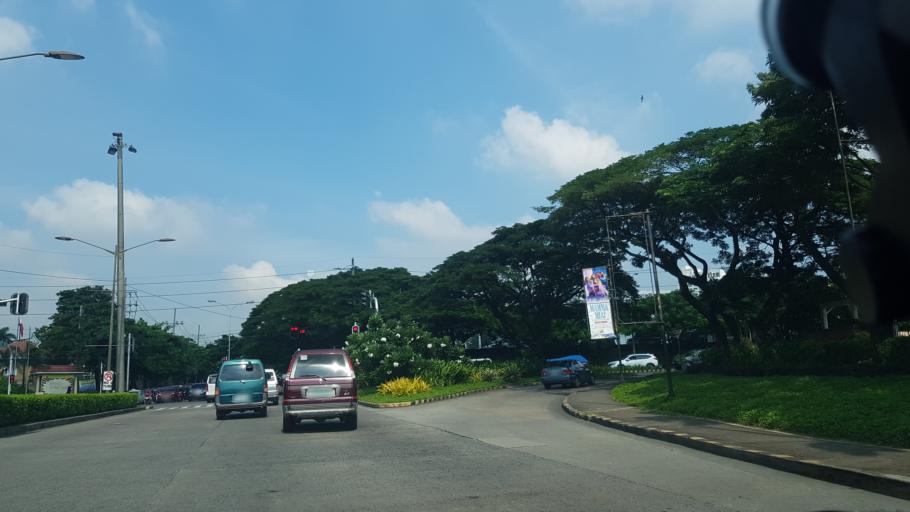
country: PH
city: Sambayanihan People's Village
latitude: 14.4225
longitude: 121.0276
